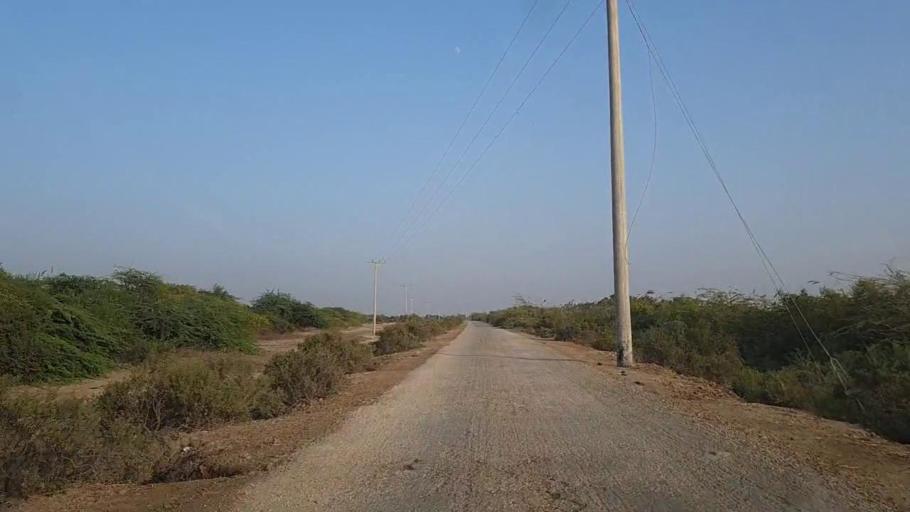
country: PK
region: Sindh
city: Keti Bandar
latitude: 24.2804
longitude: 67.6253
